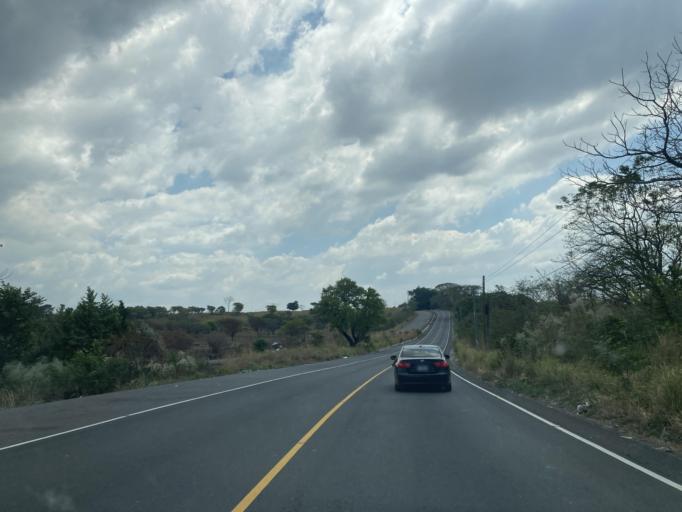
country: GT
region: Santa Rosa
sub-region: Municipio de Taxisco
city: Taxisco
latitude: 14.0933
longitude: -90.5222
